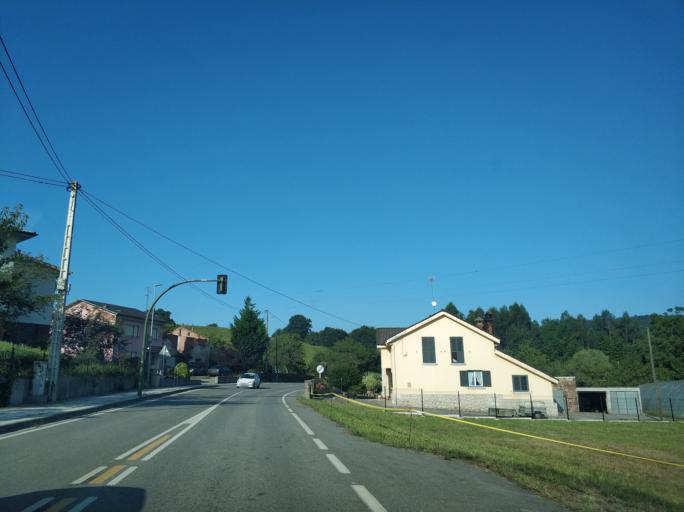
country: ES
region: Cantabria
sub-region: Provincia de Cantabria
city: Miengo
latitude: 43.3884
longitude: -3.9577
